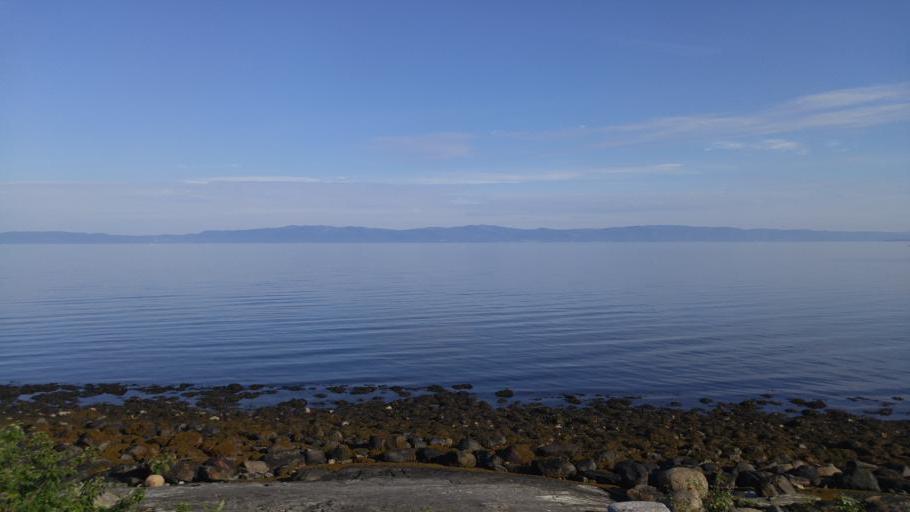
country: NO
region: Sor-Trondelag
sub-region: Malvik
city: Malvik
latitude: 63.4380
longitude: 10.5842
